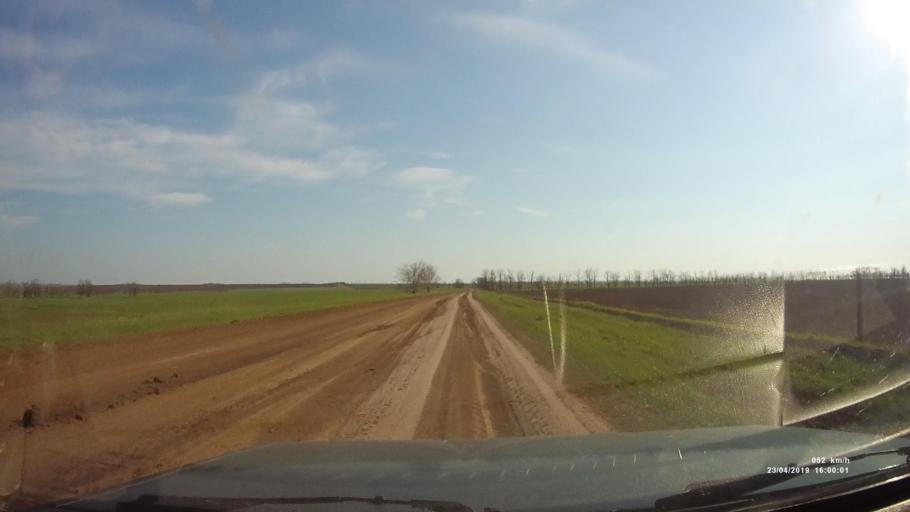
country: RU
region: Rostov
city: Remontnoye
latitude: 46.5124
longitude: 43.1089
